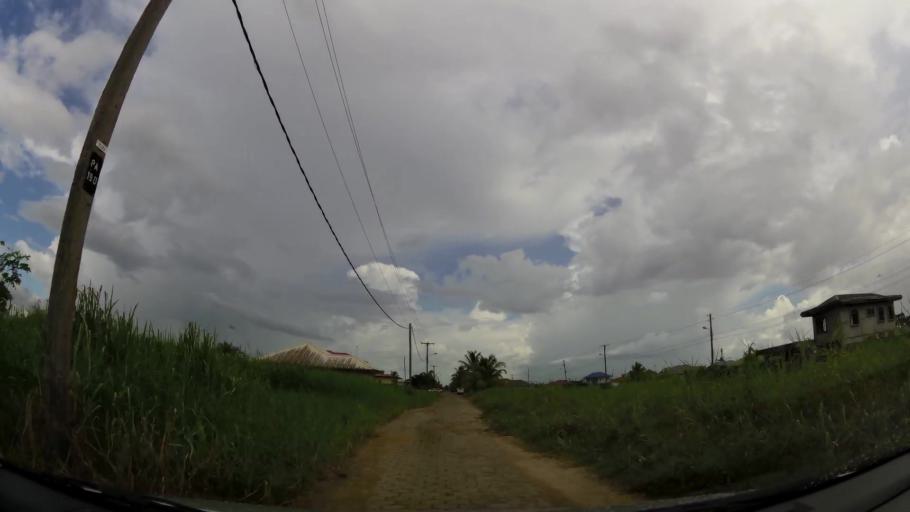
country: SR
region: Commewijne
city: Nieuw Amsterdam
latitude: 5.8622
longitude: -55.1206
